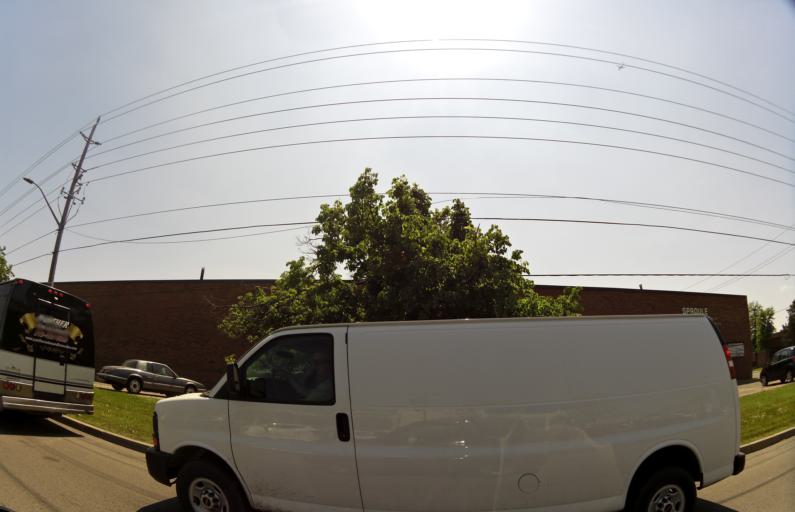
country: CA
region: Ontario
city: Mississauga
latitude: 43.6436
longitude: -79.6377
